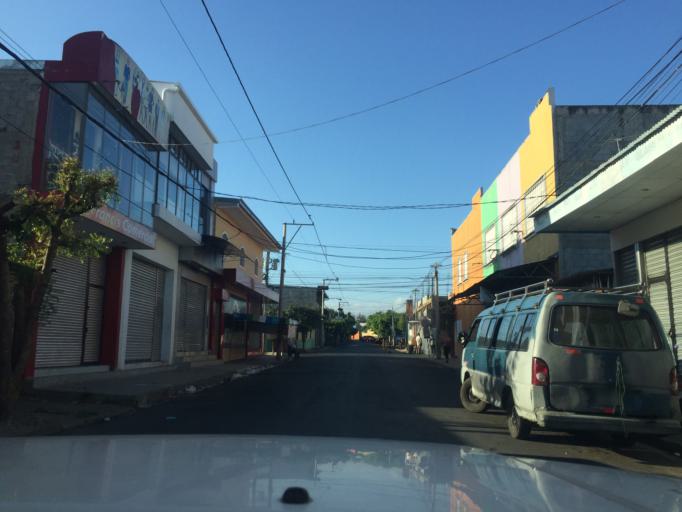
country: NI
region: Managua
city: Managua
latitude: 12.1494
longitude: -86.2550
